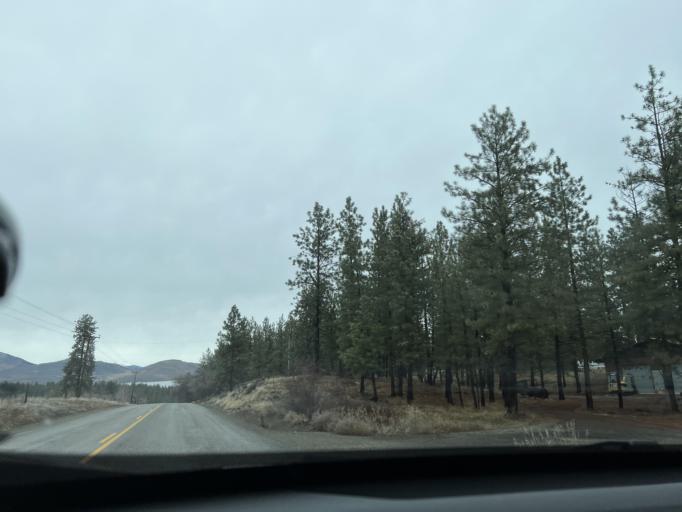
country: US
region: Washington
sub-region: Okanogan County
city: Brewster
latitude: 48.4565
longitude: -120.2057
